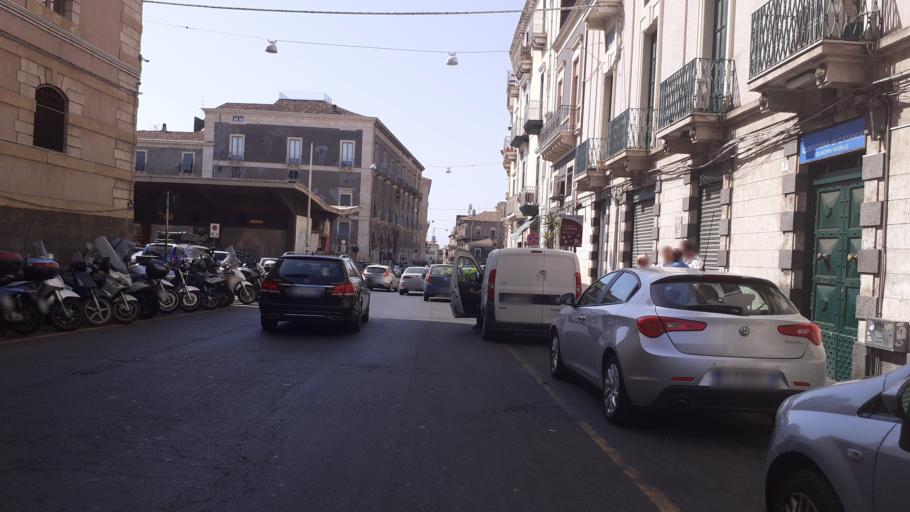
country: IT
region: Sicily
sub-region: Catania
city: Catania
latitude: 37.5048
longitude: 15.0933
